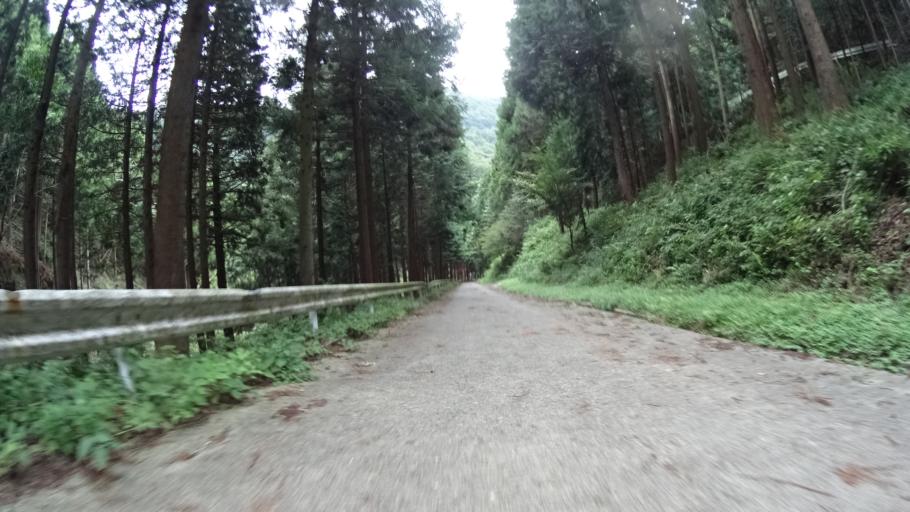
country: JP
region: Kanagawa
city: Atsugi
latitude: 35.5145
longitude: 139.2704
